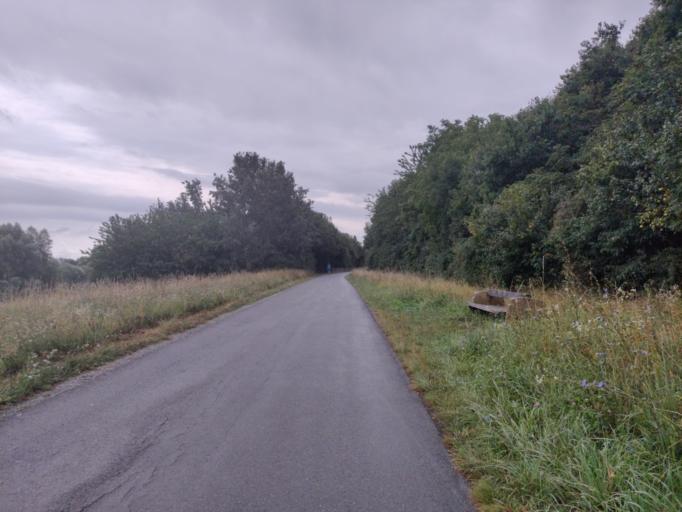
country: AT
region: Lower Austria
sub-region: Politischer Bezirk Korneuburg
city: Langenzersdorf
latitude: 48.2939
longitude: 16.3494
